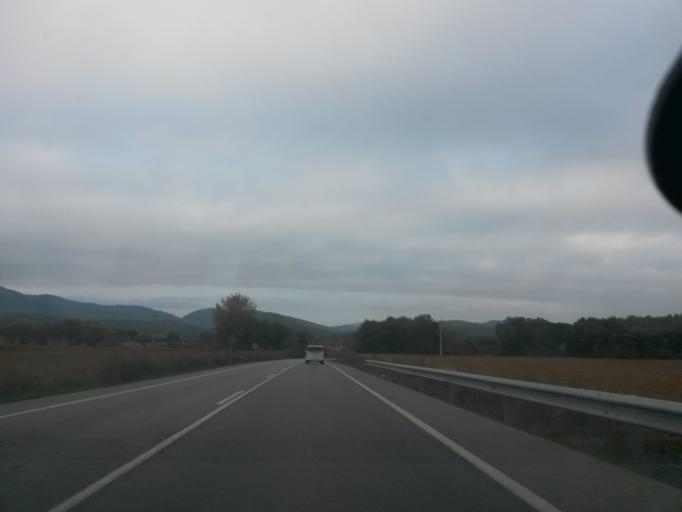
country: ES
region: Catalonia
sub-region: Provincia de Girona
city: Banyoles
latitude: 42.1533
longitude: 2.7557
